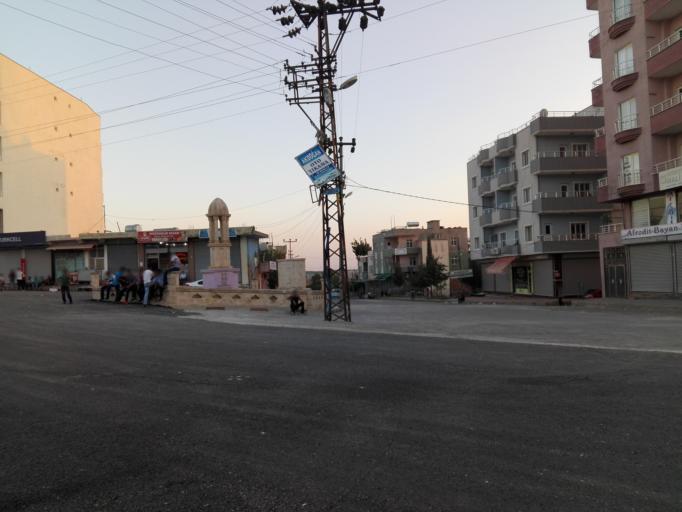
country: TR
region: Mardin
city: Dargecit
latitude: 37.5460
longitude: 41.7207
